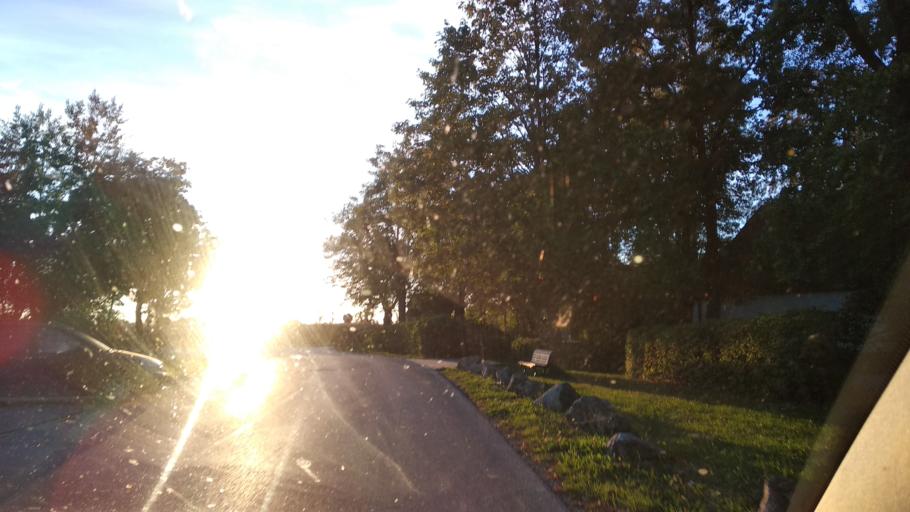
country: DE
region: Bavaria
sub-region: Upper Bavaria
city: Zorneding
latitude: 48.0792
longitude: 11.8260
